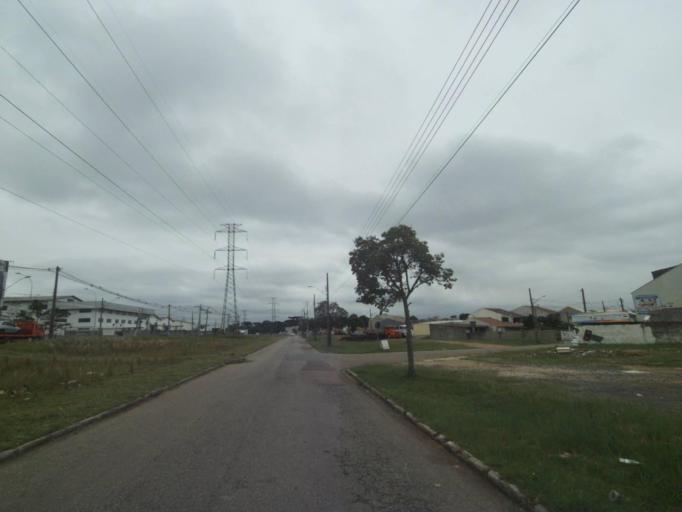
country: BR
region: Parana
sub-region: Araucaria
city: Araucaria
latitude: -25.5394
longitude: -49.3353
